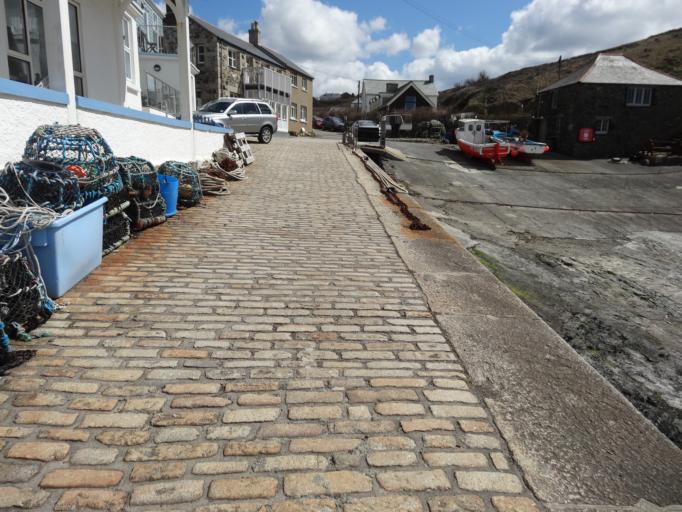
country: GB
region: England
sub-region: Cornwall
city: Mullion
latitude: 50.0155
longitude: -5.2580
